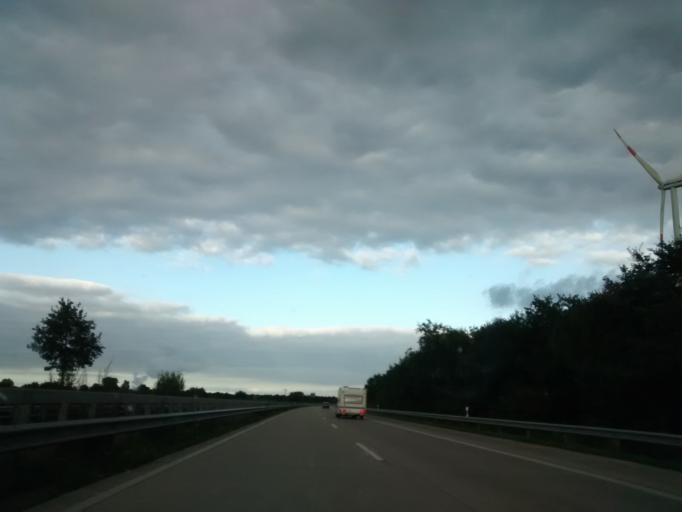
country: DE
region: Lower Saxony
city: Isterberg
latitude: 52.3302
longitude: 7.0788
